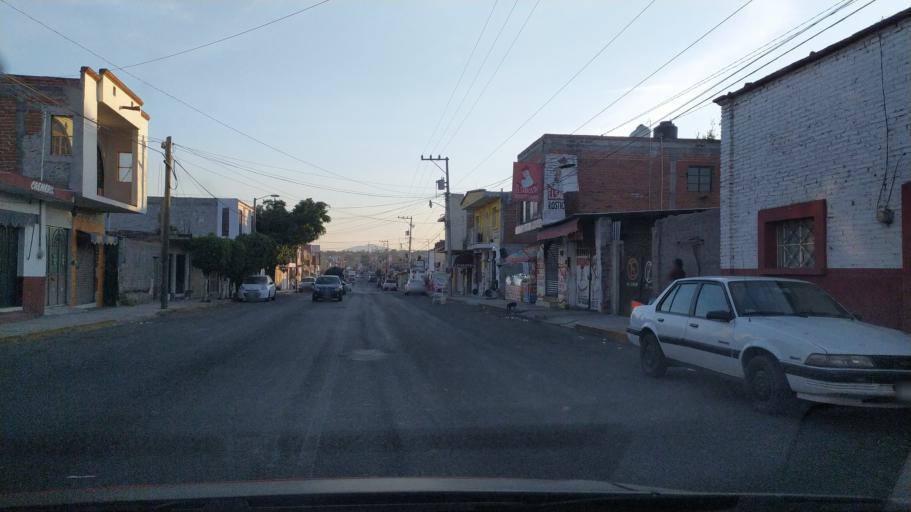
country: MX
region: Michoacan
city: Vistahermosa de Negrete
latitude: 20.2709
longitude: -102.4739
